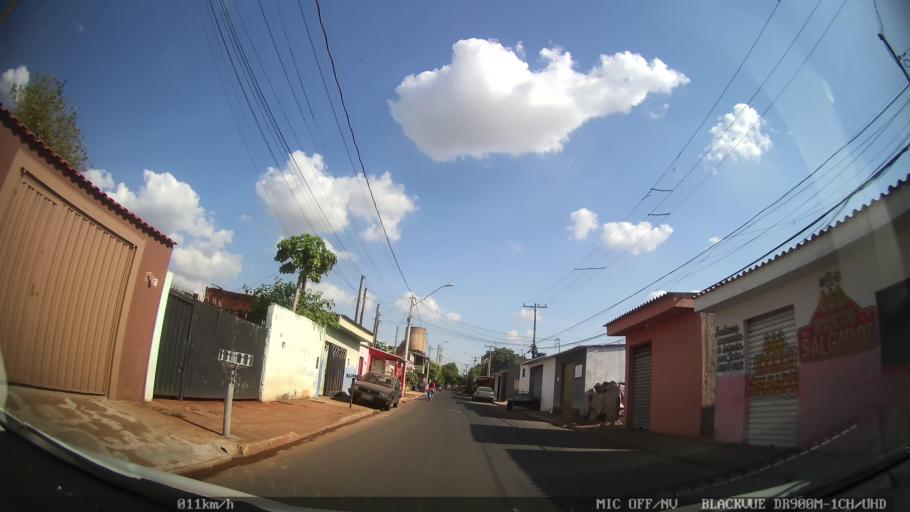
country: BR
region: Sao Paulo
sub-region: Ribeirao Preto
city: Ribeirao Preto
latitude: -21.2045
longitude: -47.8523
